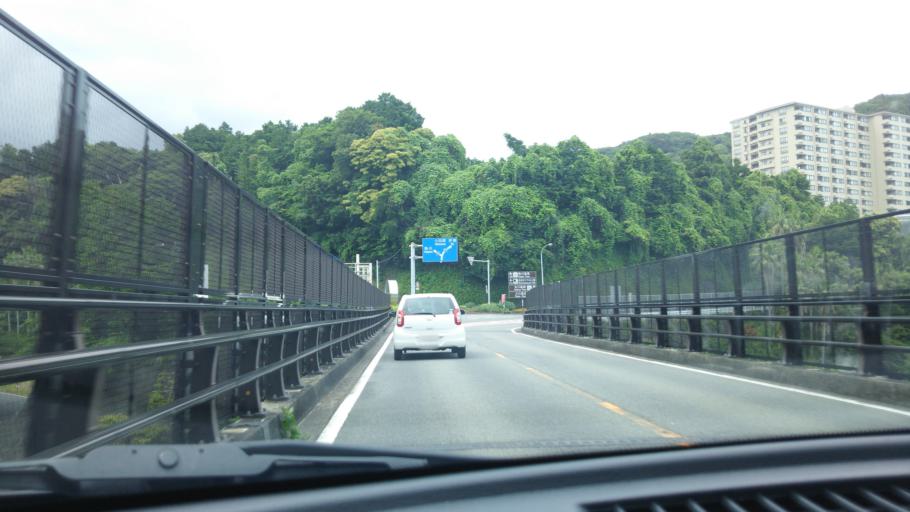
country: JP
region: Shizuoka
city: Ito
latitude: 34.8157
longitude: 139.0673
